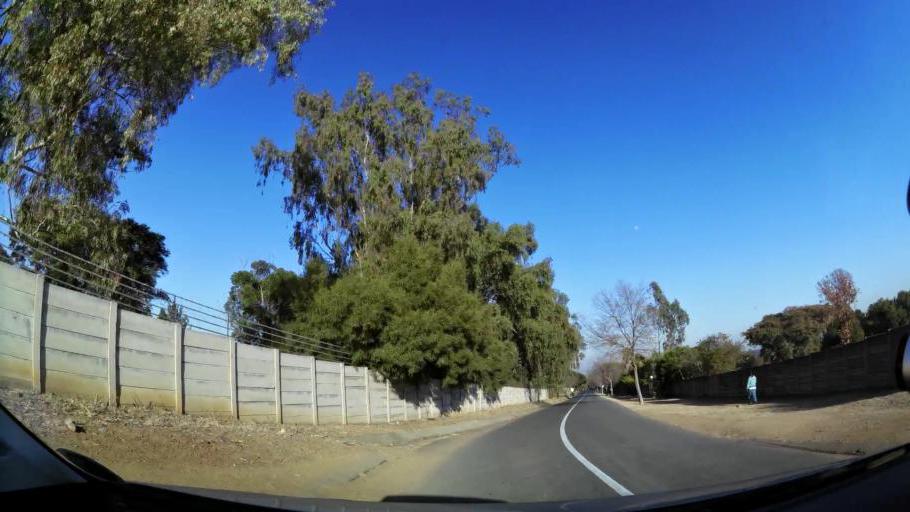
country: ZA
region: Gauteng
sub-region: City of Johannesburg Metropolitan Municipality
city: Midrand
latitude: -26.0217
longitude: 28.1452
